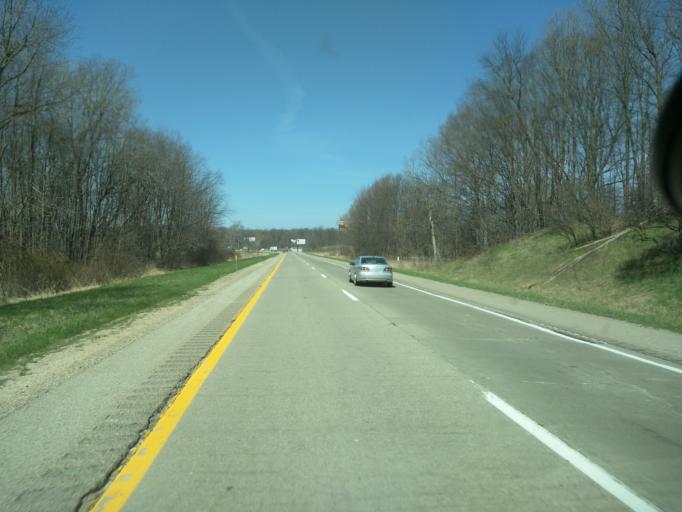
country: US
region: Michigan
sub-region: Ionia County
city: Saranac
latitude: 42.8796
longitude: -85.2754
